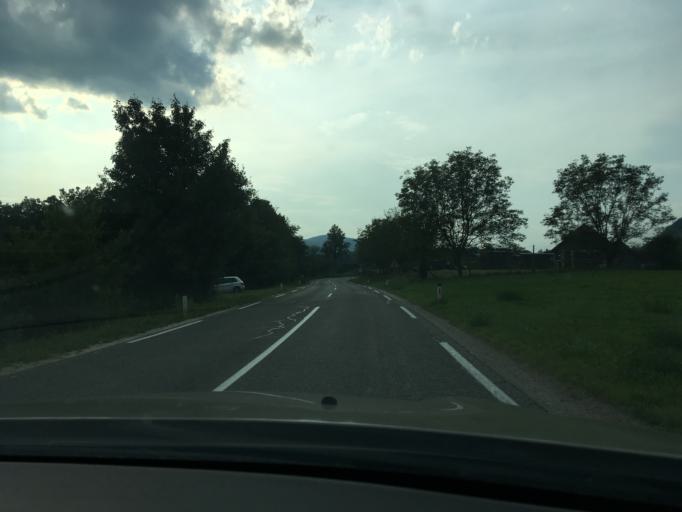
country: SI
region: Zuzemberk
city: Zuzemberk
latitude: 45.7949
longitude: 14.9856
